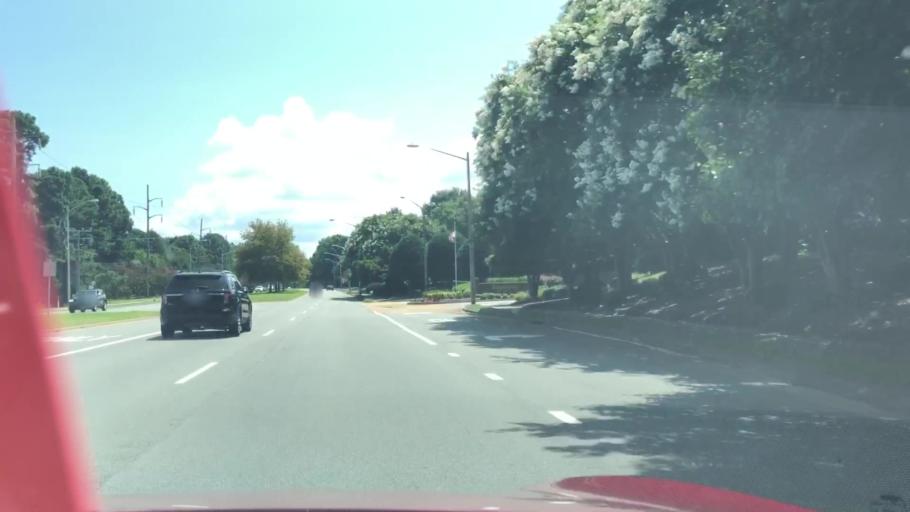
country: US
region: Virginia
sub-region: City of Virginia Beach
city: Virginia Beach
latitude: 36.8955
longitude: -76.0609
